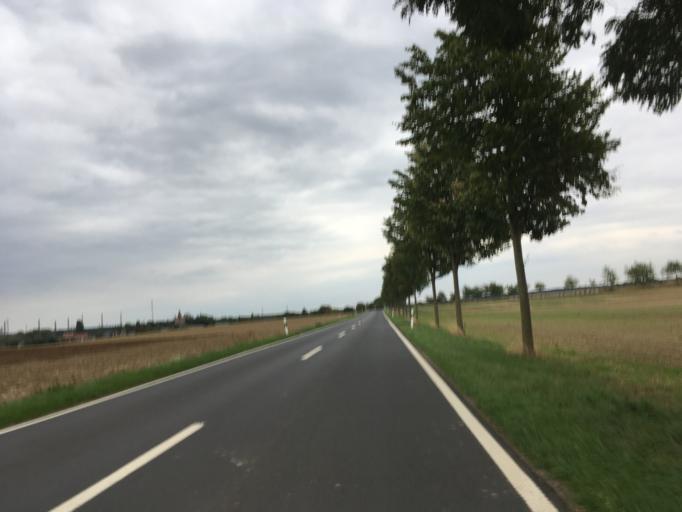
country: DE
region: Brandenburg
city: Meyenburg
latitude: 53.0875
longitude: 14.1902
